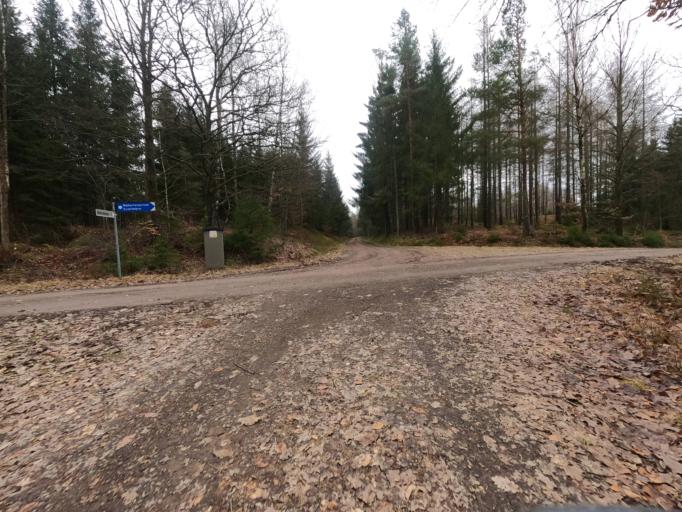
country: SE
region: Kronoberg
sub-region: Markaryds Kommun
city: Stromsnasbruk
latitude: 56.7905
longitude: 13.6279
